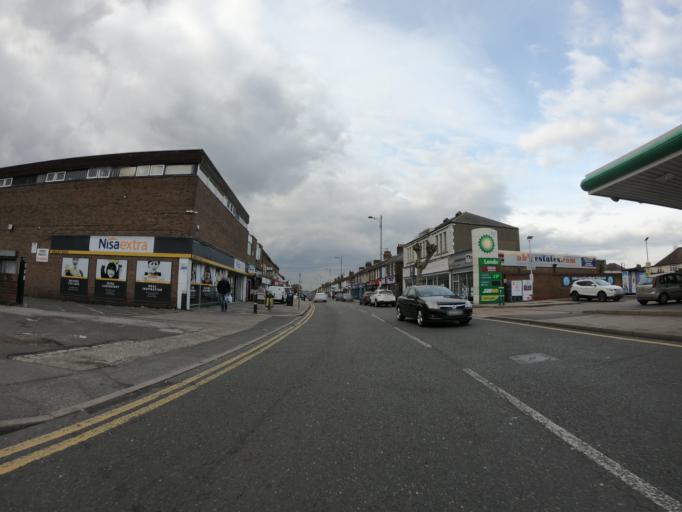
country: GB
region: England
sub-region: Greater London
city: Erith
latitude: 51.4729
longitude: 0.1624
